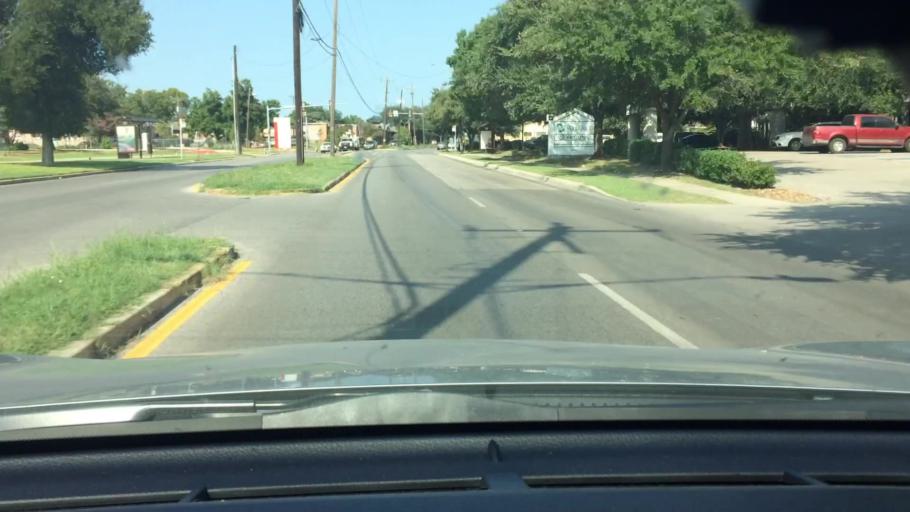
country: US
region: Texas
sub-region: Bexar County
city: China Grove
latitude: 29.3750
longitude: -98.4113
